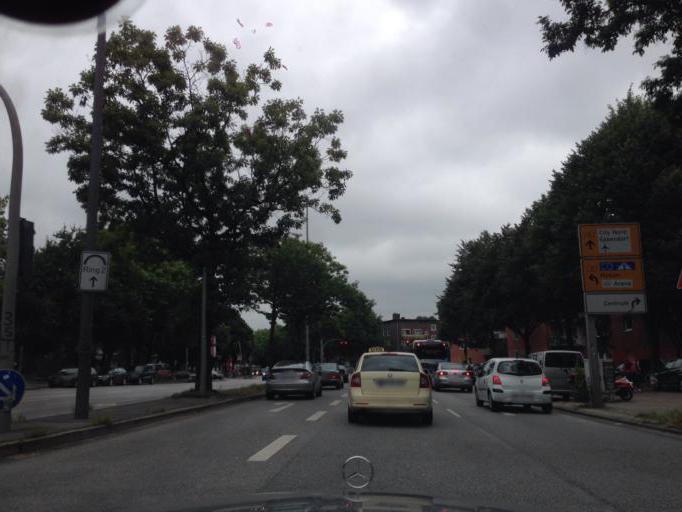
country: DE
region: Hamburg
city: St. Pauli
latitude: 53.5695
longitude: 9.9547
